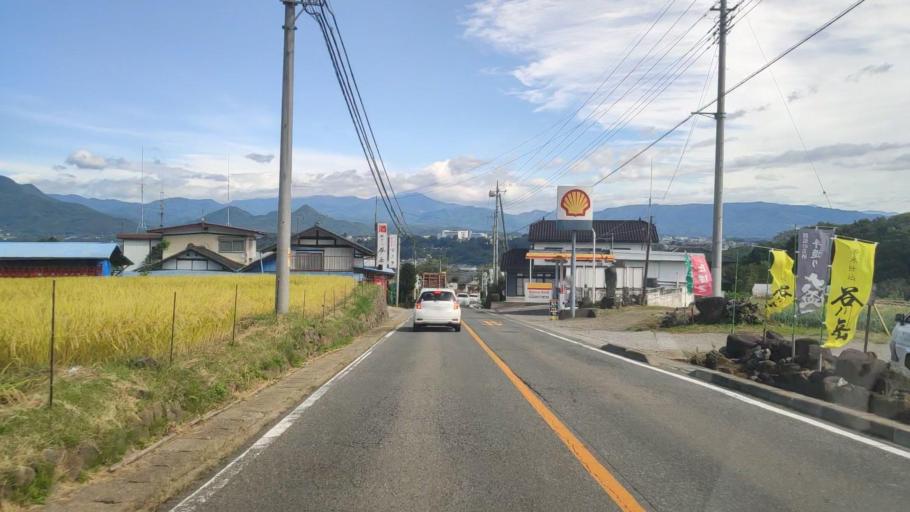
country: JP
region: Gunma
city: Numata
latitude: 36.6265
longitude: 139.0287
